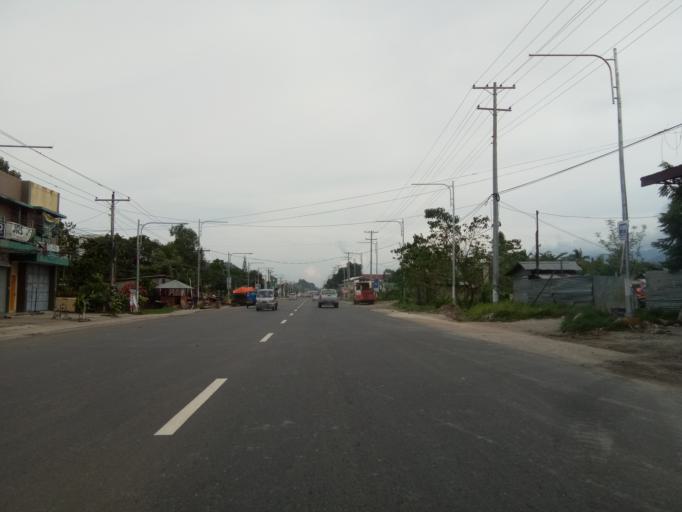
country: PH
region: Caraga
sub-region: Province of Surigao del Norte
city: Rizal
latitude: 9.7681
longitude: 125.4833
